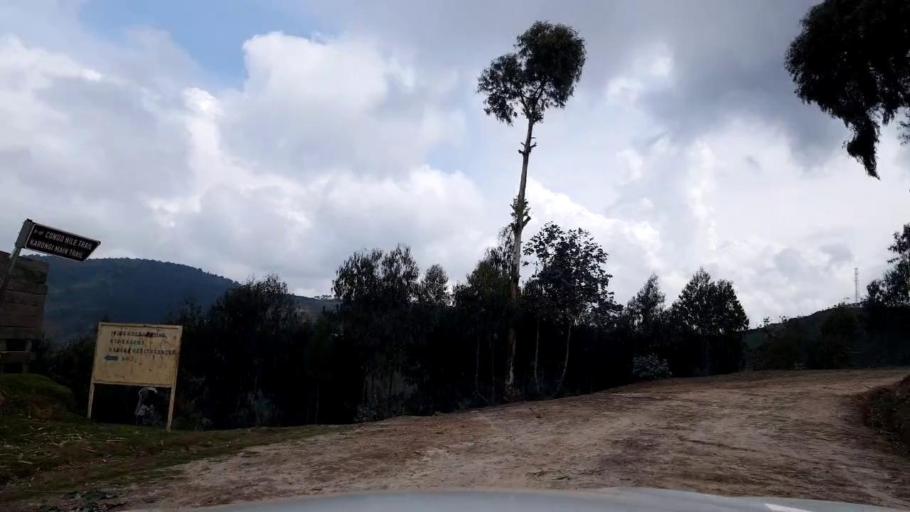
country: RW
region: Western Province
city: Kibuye
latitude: -1.9571
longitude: 29.4780
